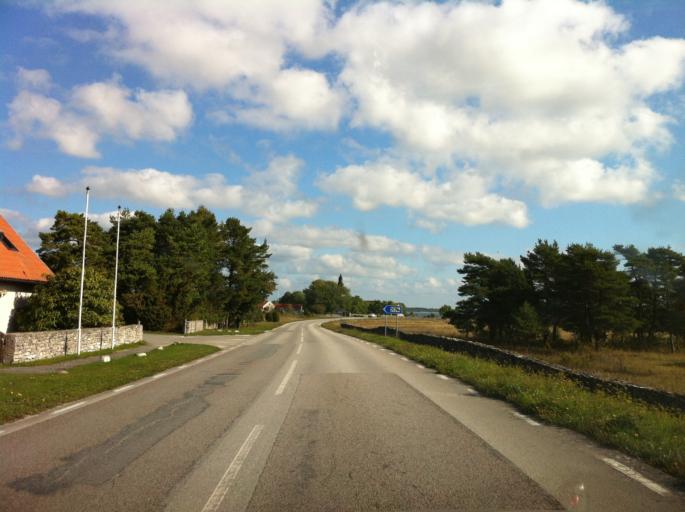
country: SE
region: Gotland
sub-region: Gotland
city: Slite
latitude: 57.9131
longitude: 19.1269
